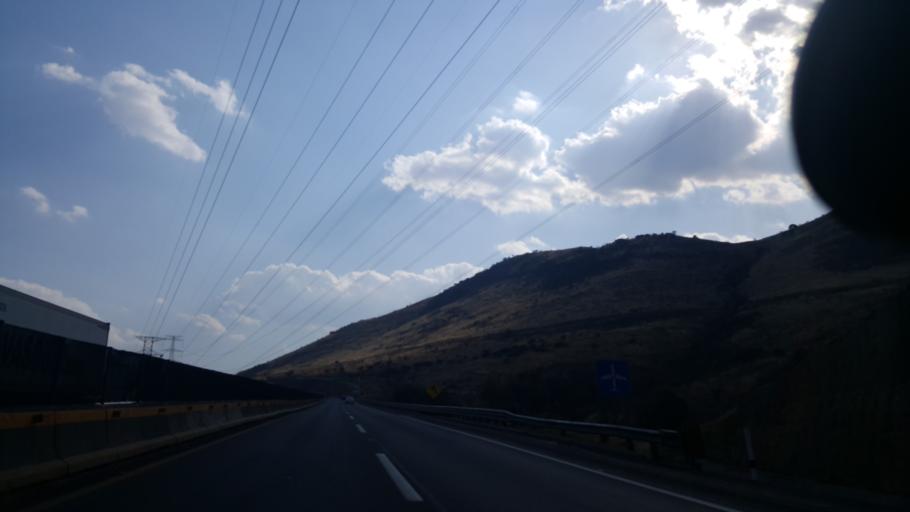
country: MX
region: Mexico
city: Ciudad Lopez Mateos
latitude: 19.5610
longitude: -99.2754
